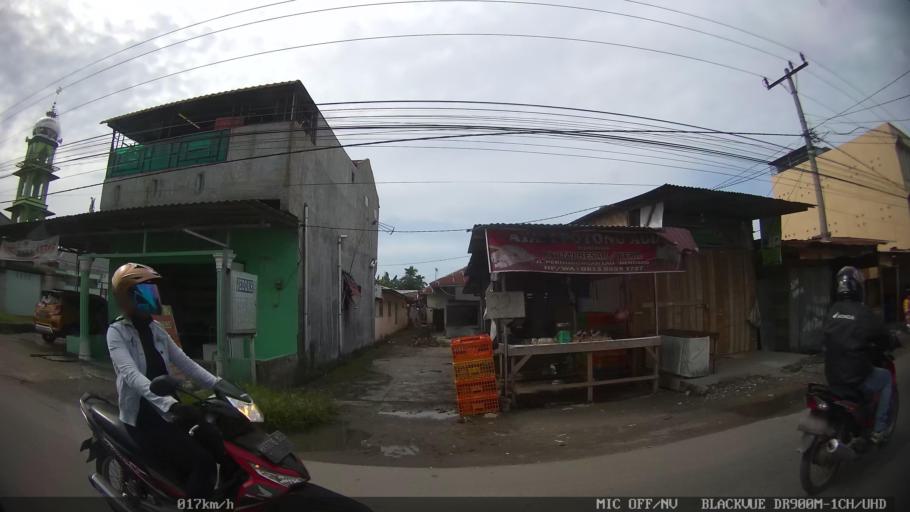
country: ID
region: North Sumatra
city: Medan
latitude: 3.6208
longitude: 98.7250
